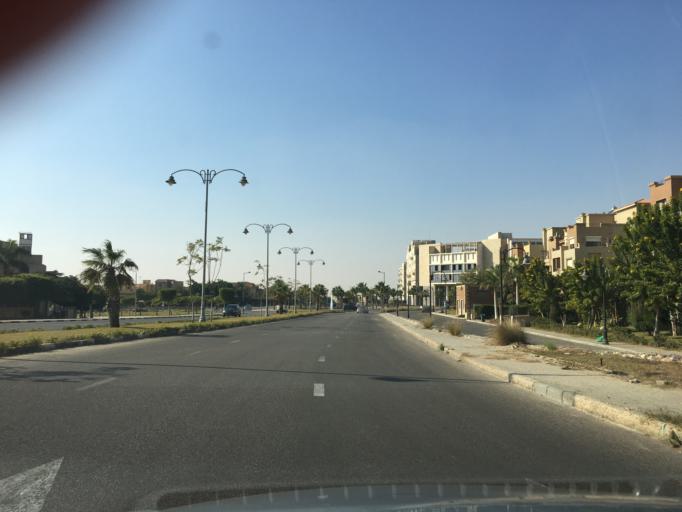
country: EG
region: Al Jizah
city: Awsim
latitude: 30.0653
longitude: 30.9486
